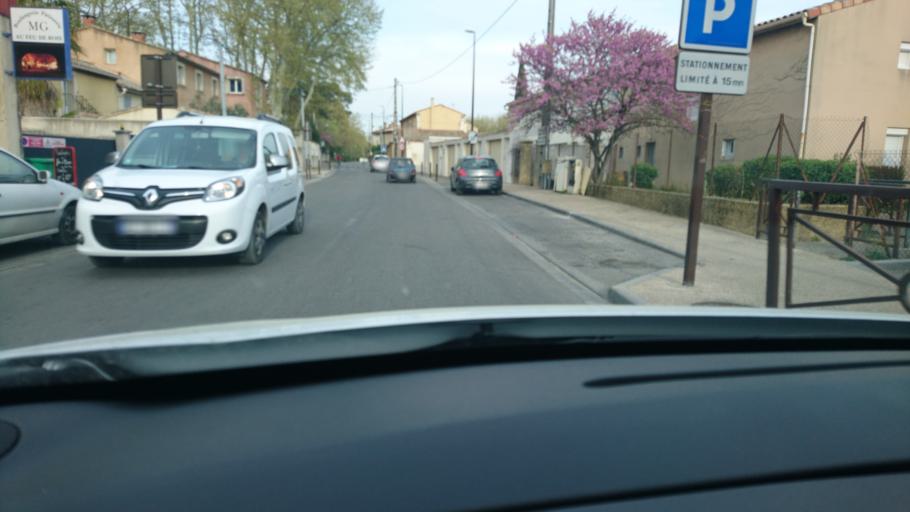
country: FR
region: Provence-Alpes-Cote d'Azur
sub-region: Departement du Vaucluse
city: Montfavet
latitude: 43.9371
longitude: 4.8788
